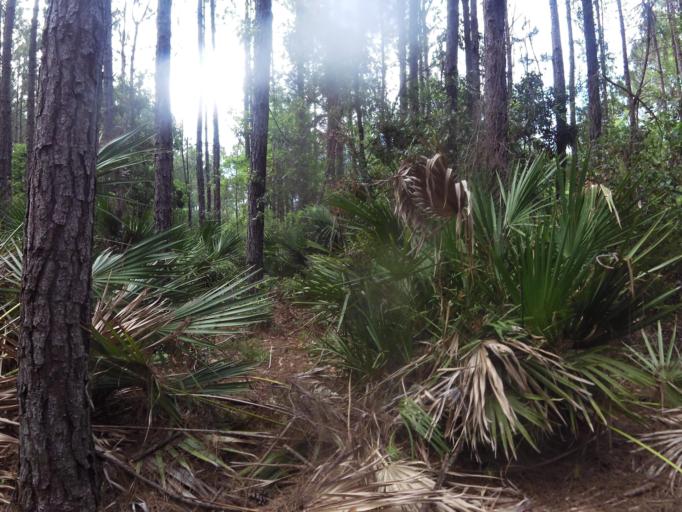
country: US
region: Florida
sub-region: Duval County
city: Atlantic Beach
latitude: 30.4563
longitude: -81.4737
